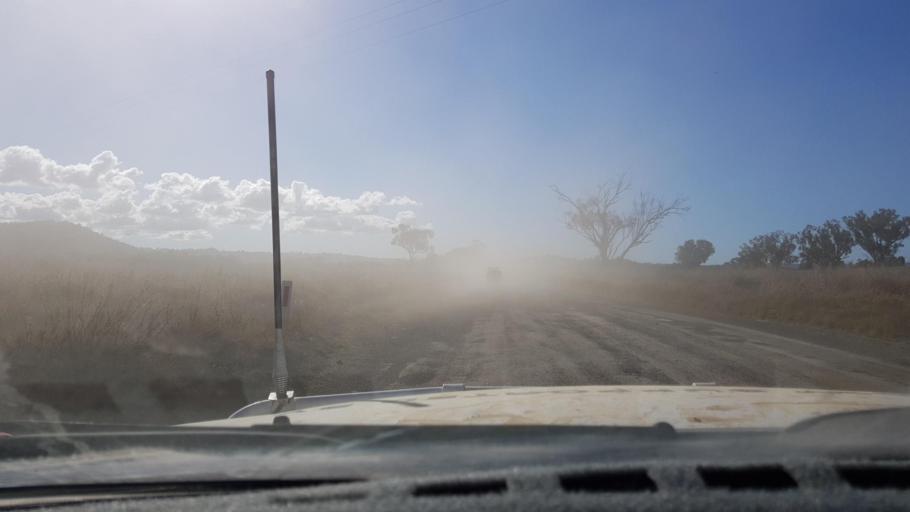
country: AU
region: New South Wales
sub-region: Narrabri
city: Blair Athol
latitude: -30.6718
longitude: 150.4524
